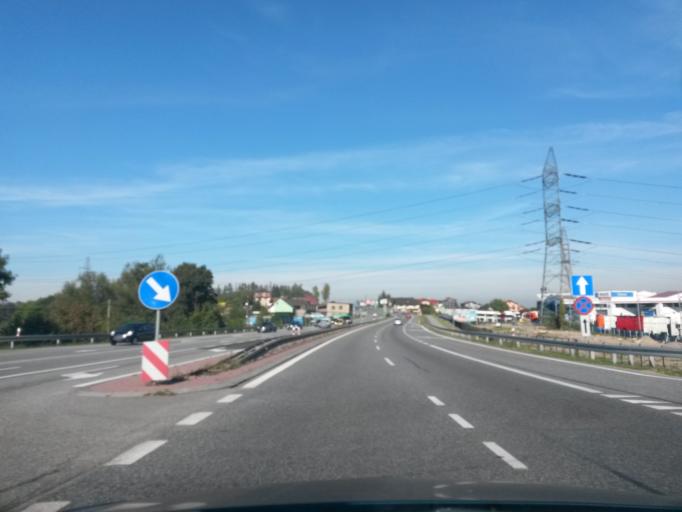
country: PL
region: Lesser Poland Voivodeship
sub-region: Powiat krakowski
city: Mogilany
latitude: 49.9514
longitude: 19.8900
